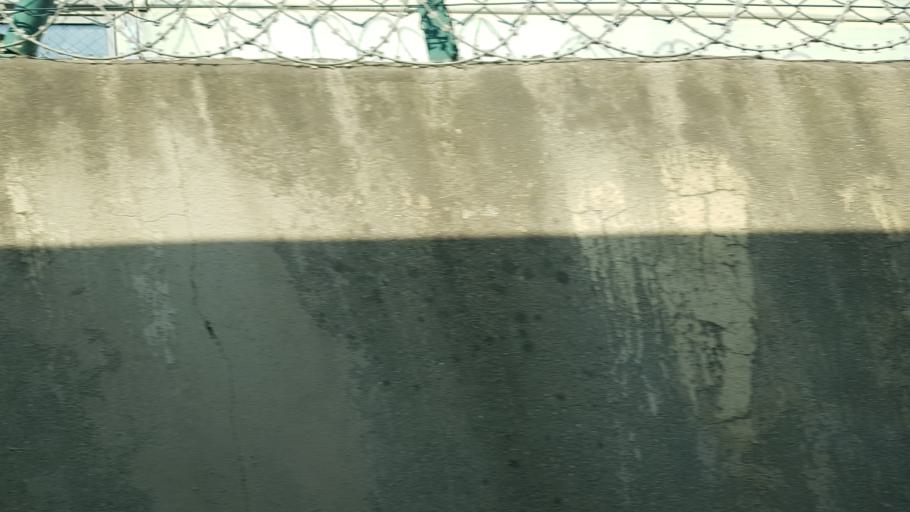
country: TR
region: Istanbul
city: Maltepe
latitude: 40.8996
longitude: 29.2016
